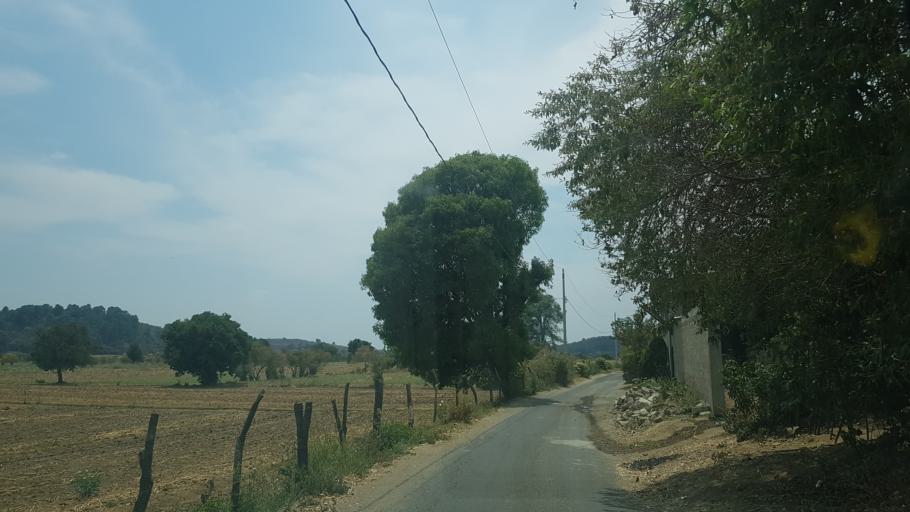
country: MX
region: Puebla
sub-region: Atzitzihuacan
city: Santiago Atzitzihuacan
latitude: 18.8639
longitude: -98.6110
